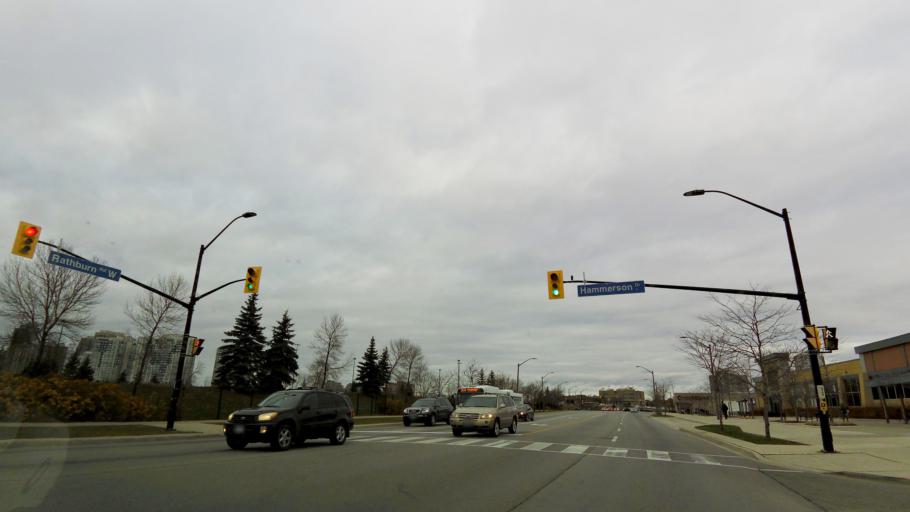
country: CA
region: Ontario
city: Mississauga
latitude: 43.5956
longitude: -79.6456
